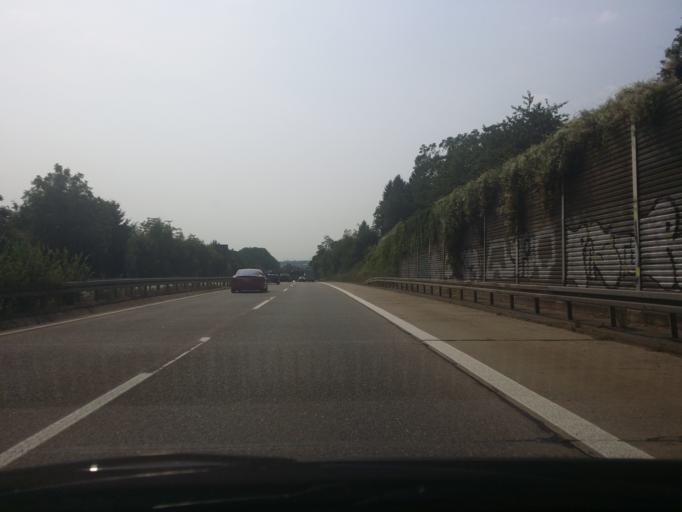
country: DE
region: Rheinland-Pfalz
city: Budenheim
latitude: 50.0518
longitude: 8.1967
